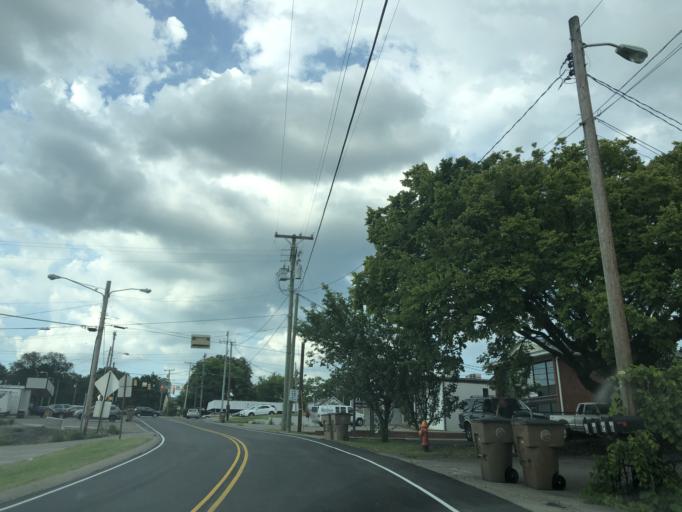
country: US
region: Tennessee
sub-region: Davidson County
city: Lakewood
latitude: 36.1688
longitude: -86.6745
